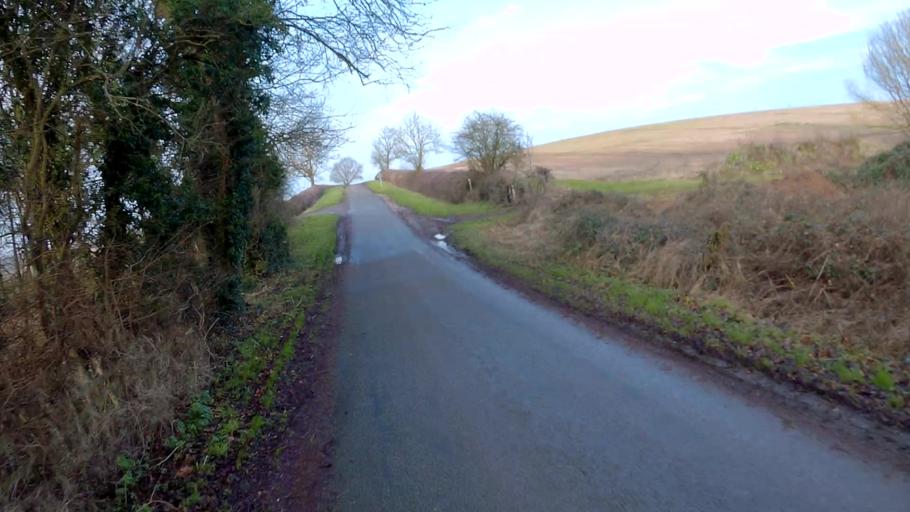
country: GB
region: England
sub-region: Lincolnshire
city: Bourne
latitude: 52.7553
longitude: -0.4177
